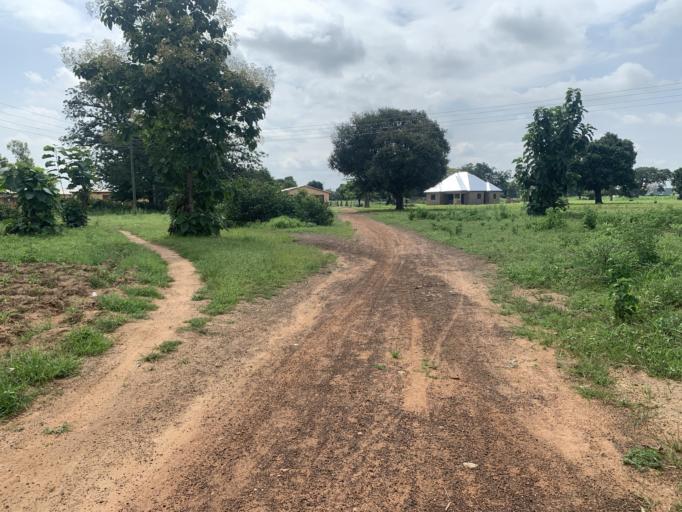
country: GH
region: Upper East
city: Navrongo
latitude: 10.8681
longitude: -1.0615
